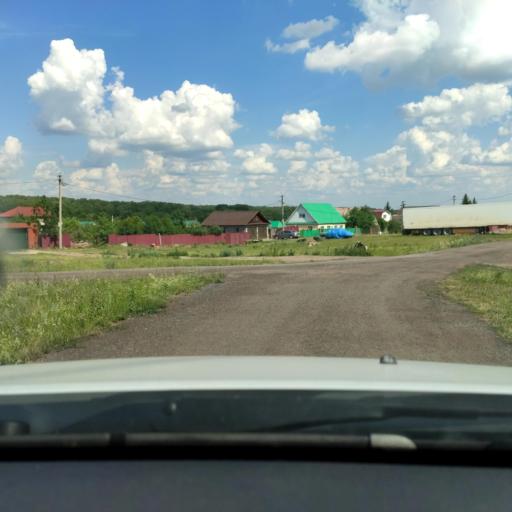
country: RU
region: Bashkortostan
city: Avdon
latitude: 54.7095
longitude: 55.7339
